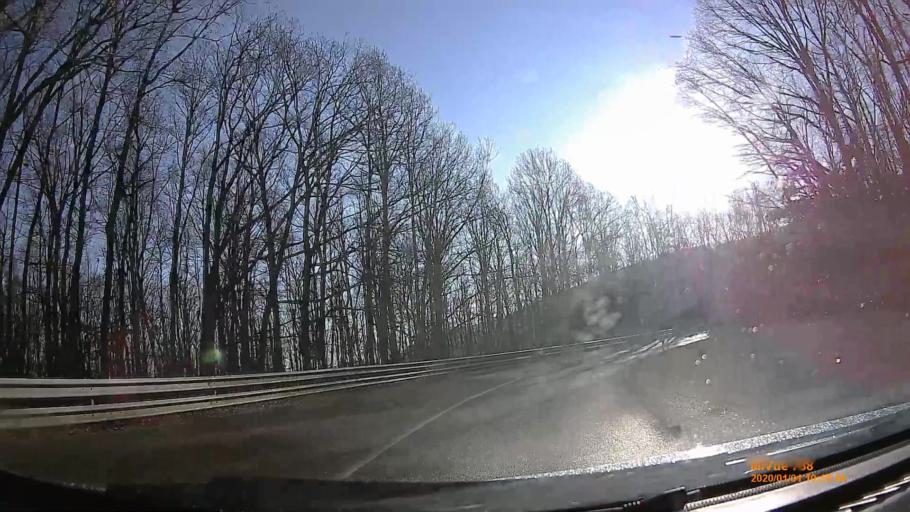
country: HU
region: Heves
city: Paradsasvar
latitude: 47.9051
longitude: 19.9961
